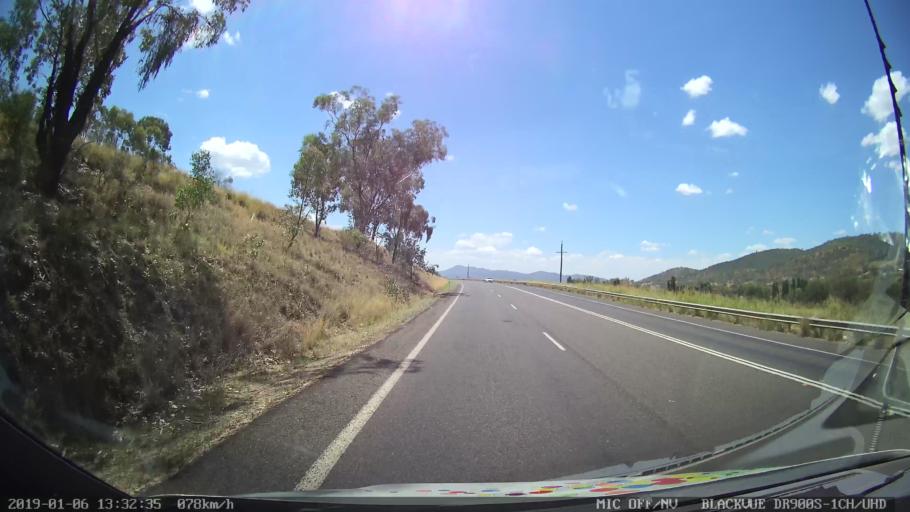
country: AU
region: New South Wales
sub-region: Tamworth Municipality
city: East Tamworth
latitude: -31.1086
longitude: 150.9996
